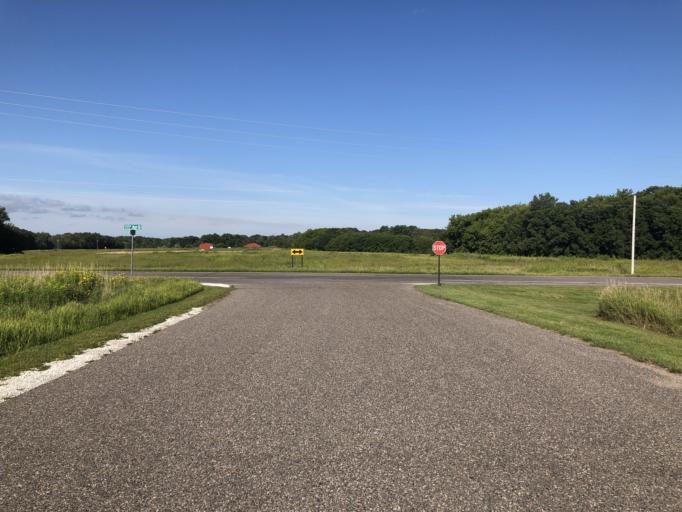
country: US
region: Minnesota
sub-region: Sherburne County
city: Becker
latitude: 45.4243
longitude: -93.8395
